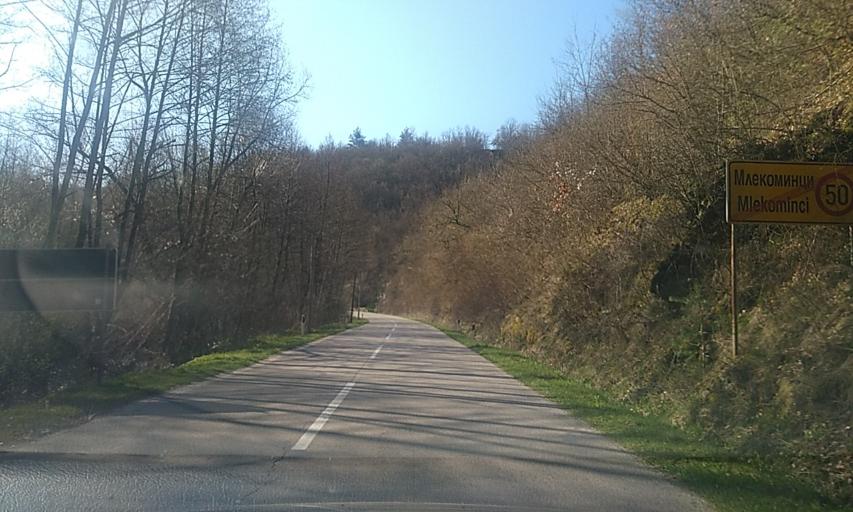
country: RS
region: Central Serbia
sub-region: Pcinjski Okrug
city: Bosilegrad
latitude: 42.4462
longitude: 22.5013
